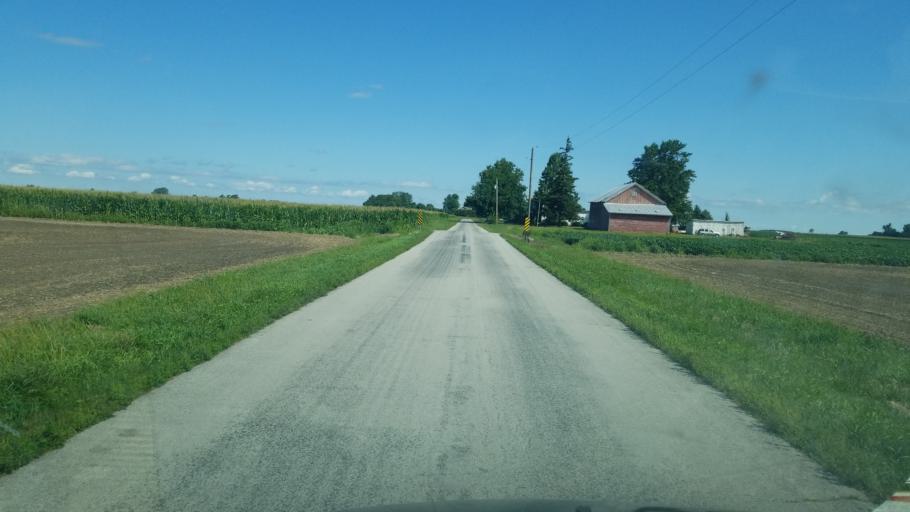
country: US
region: Ohio
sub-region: Hancock County
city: McComb
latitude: 41.1346
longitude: -83.7461
